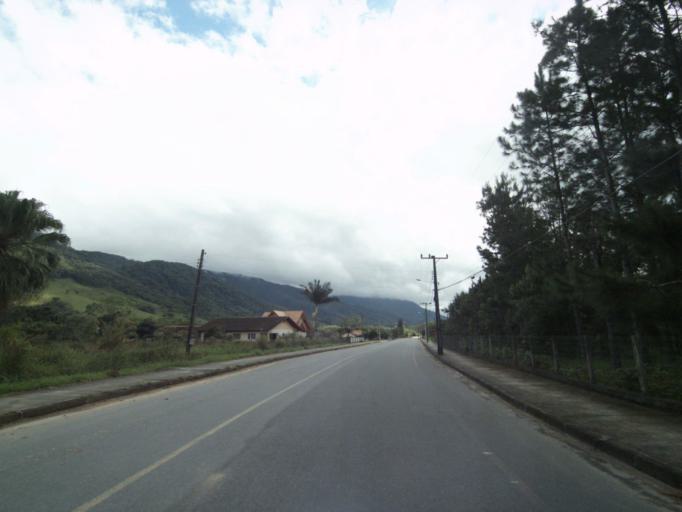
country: BR
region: Santa Catarina
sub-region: Pomerode
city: Pomerode
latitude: -26.6758
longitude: -49.1844
